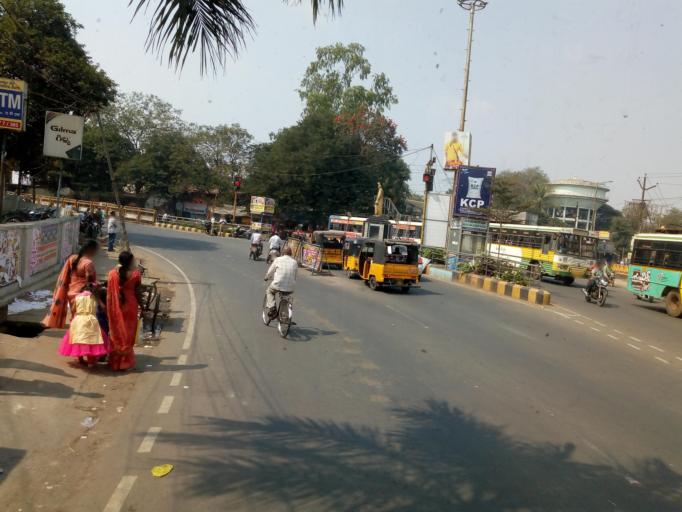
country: IN
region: Andhra Pradesh
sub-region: West Godavari
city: Eluru
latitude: 16.7106
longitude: 81.0948
